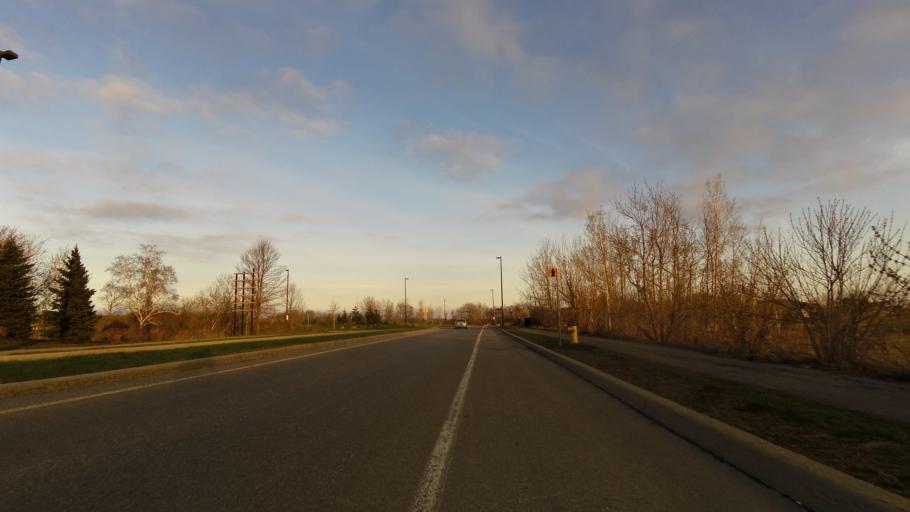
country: CA
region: Ontario
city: Bells Corners
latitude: 45.3480
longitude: -75.9037
